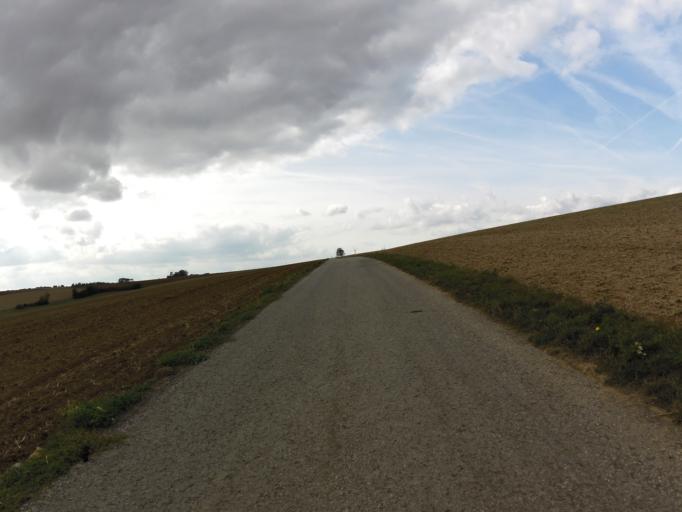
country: DE
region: Bavaria
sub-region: Regierungsbezirk Unterfranken
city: Reichenberg
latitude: 49.7100
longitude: 9.9469
